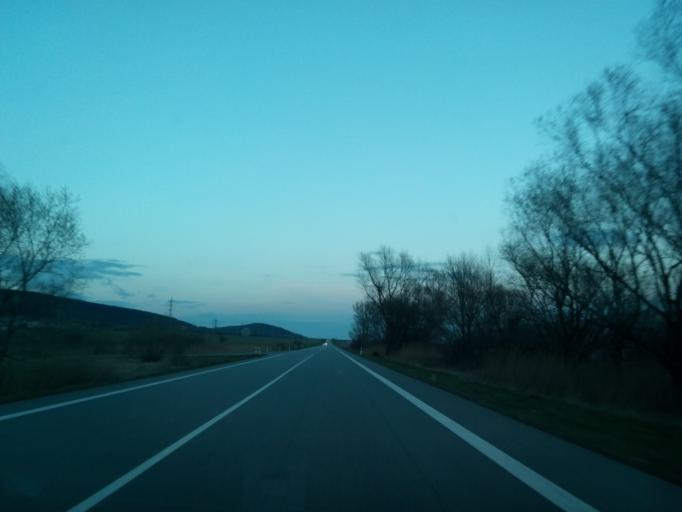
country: SK
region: Kosicky
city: Medzev
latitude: 48.6009
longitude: 20.7576
